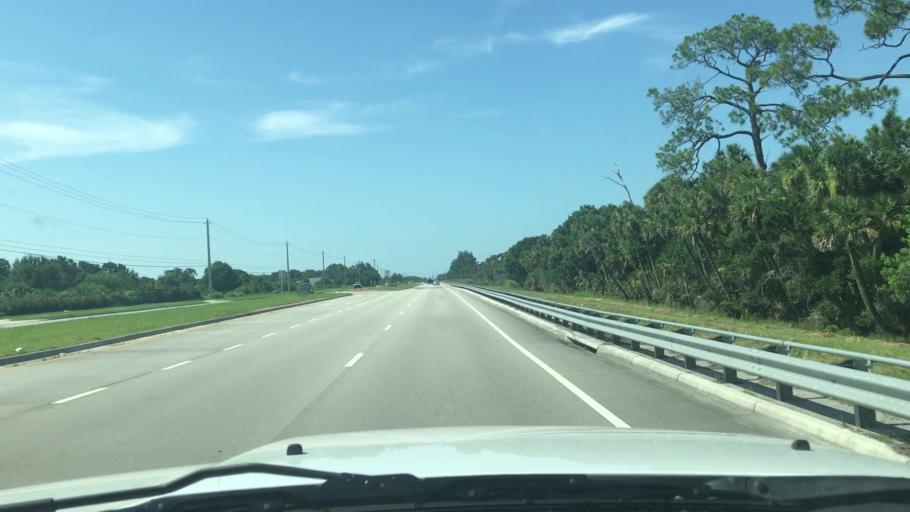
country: US
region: Florida
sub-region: Indian River County
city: West Vero Corridor
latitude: 27.6562
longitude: -80.4630
